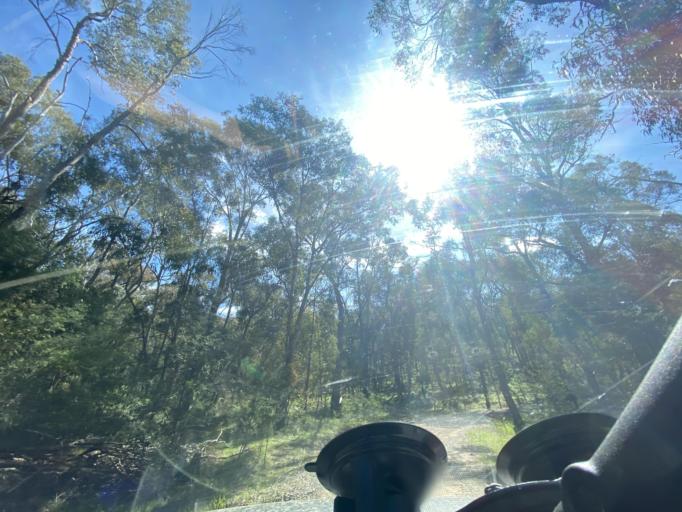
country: AU
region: Victoria
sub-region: Mansfield
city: Mansfield
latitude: -36.8016
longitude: 146.1168
